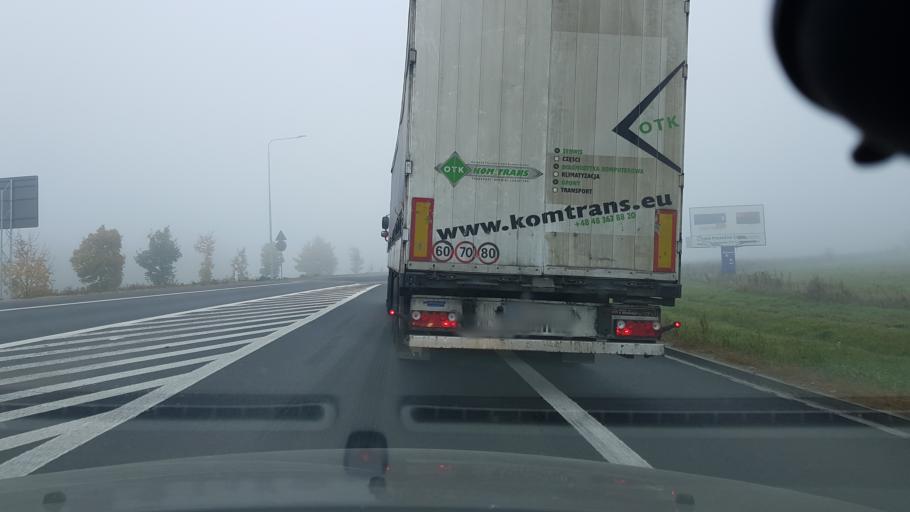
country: PL
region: Masovian Voivodeship
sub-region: Powiat zyrardowski
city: Mszczonow
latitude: 51.9927
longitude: 20.5060
